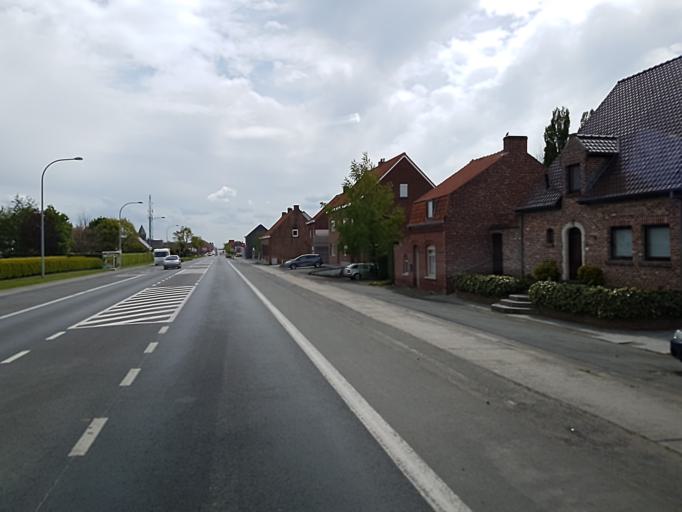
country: BE
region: Flanders
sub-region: Provincie West-Vlaanderen
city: Zonnebeke
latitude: 50.8366
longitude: 2.9848
